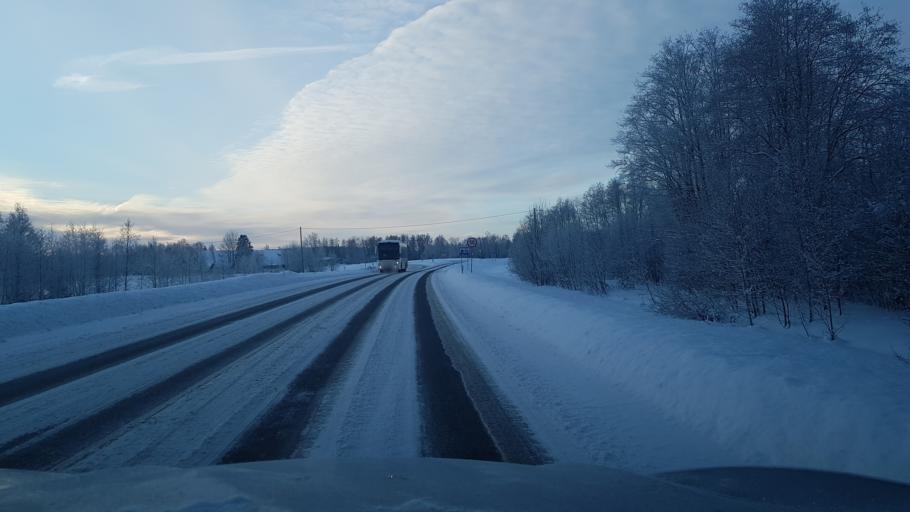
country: EE
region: Ida-Virumaa
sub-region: Johvi vald
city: Johvi
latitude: 59.3404
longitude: 27.4679
